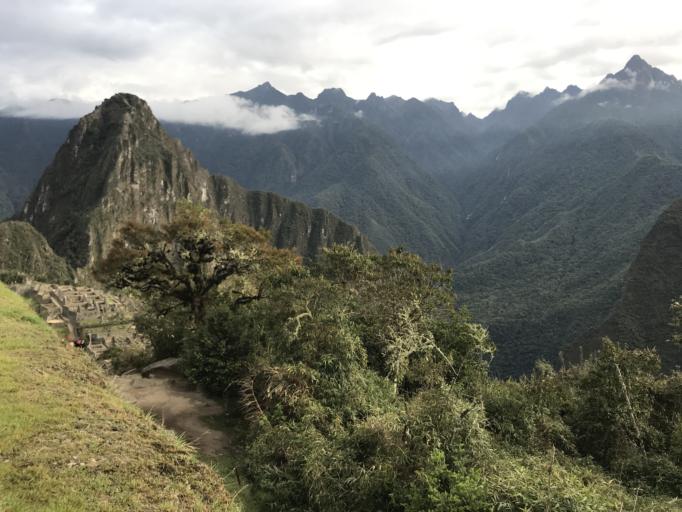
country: PE
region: Cusco
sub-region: Provincia de La Convencion
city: Santa Teresa
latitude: -13.1656
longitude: -72.5442
